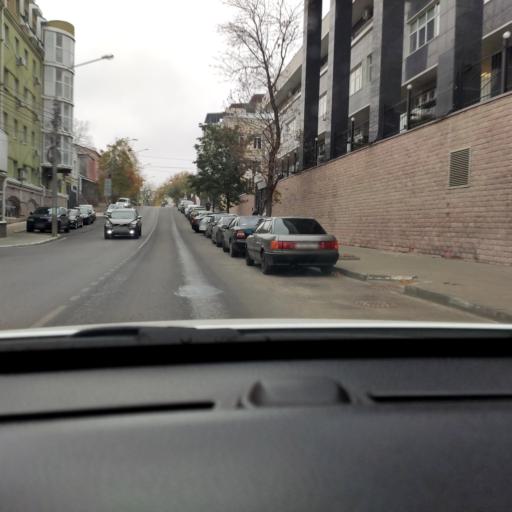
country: RU
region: Voronezj
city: Voronezh
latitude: 51.6779
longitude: 39.2184
